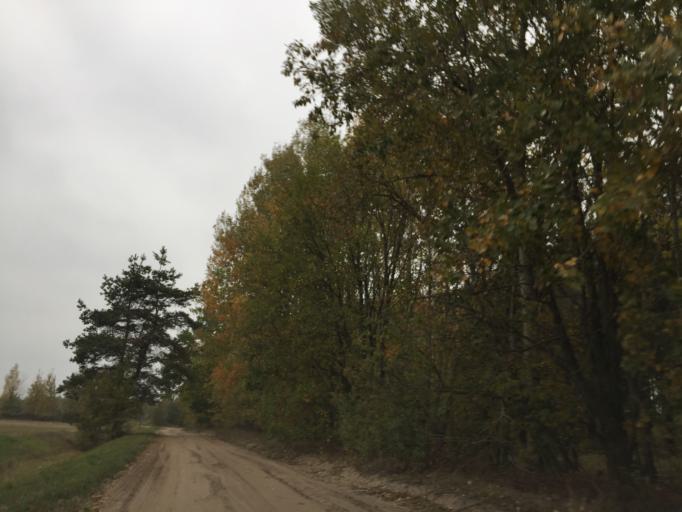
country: LV
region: Dobeles Rajons
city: Dobele
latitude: 56.6726
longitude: 23.4669
